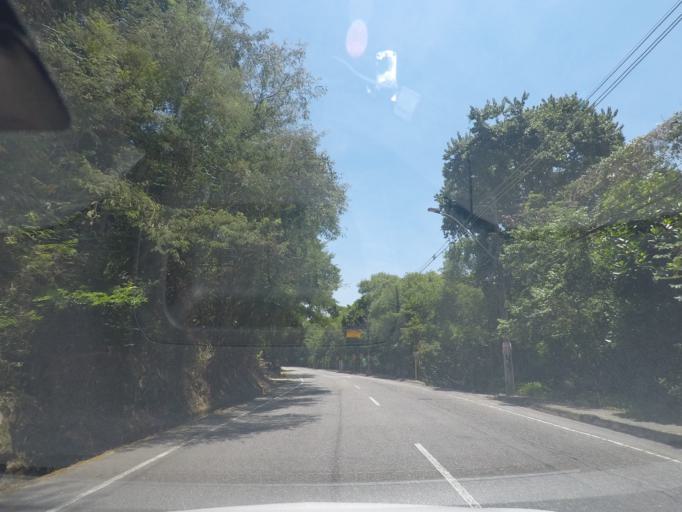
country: BR
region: Rio de Janeiro
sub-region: Niteroi
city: Niteroi
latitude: -22.9217
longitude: -43.0660
